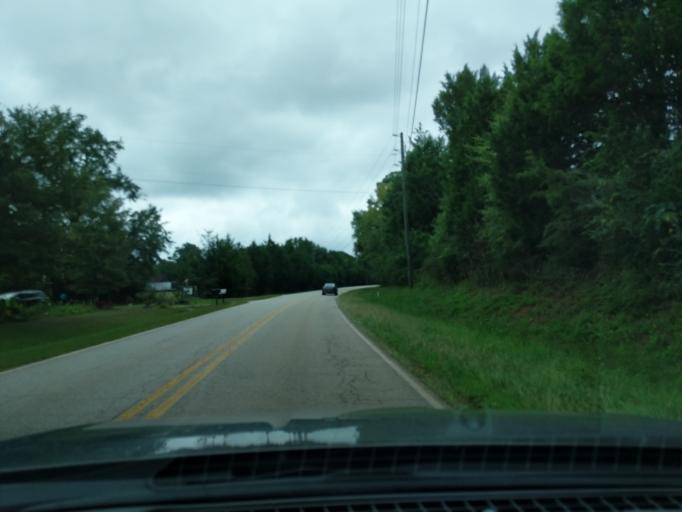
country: US
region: Georgia
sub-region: Columbia County
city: Appling
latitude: 33.6109
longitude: -82.3984
